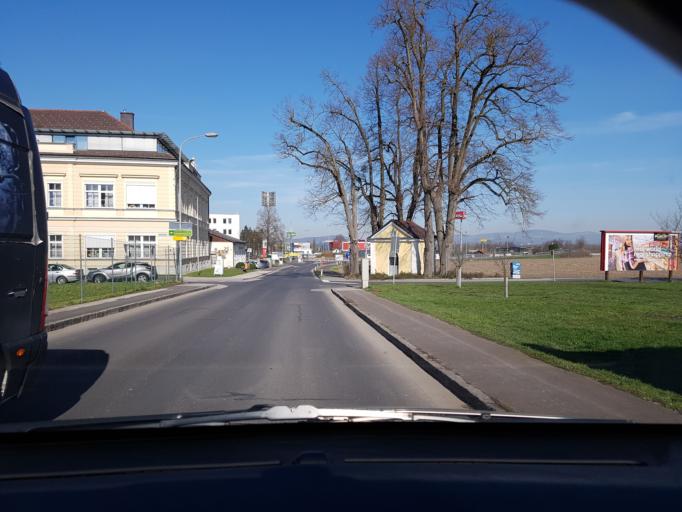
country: AT
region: Upper Austria
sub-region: Politischer Bezirk Linz-Land
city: Ansfelden
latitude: 48.2112
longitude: 14.2895
